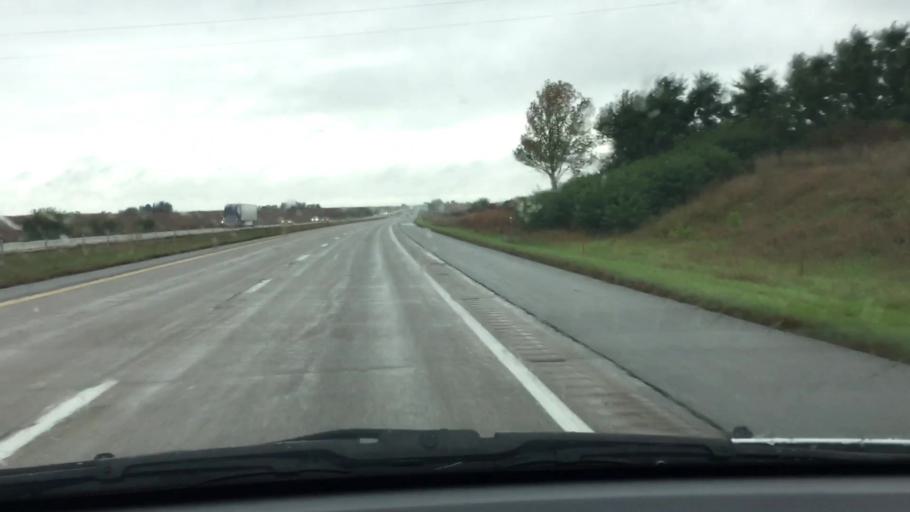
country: US
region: Iowa
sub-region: Poweshiek County
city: Brooklyn
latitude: 41.6954
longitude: -92.4546
